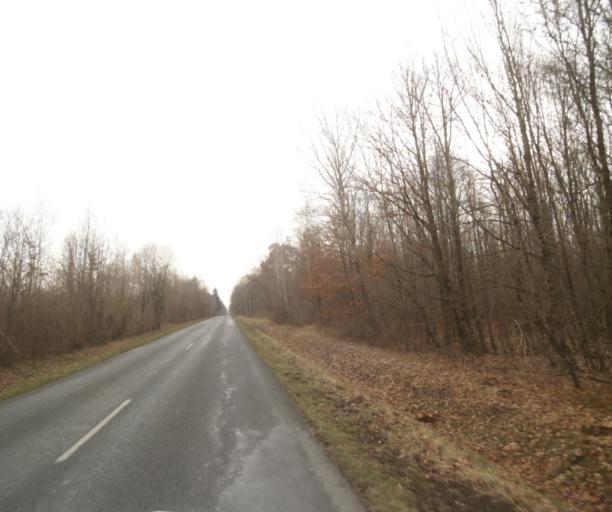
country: FR
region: Champagne-Ardenne
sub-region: Departement de la Marne
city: Pargny-sur-Saulx
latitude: 48.7229
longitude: 4.8738
